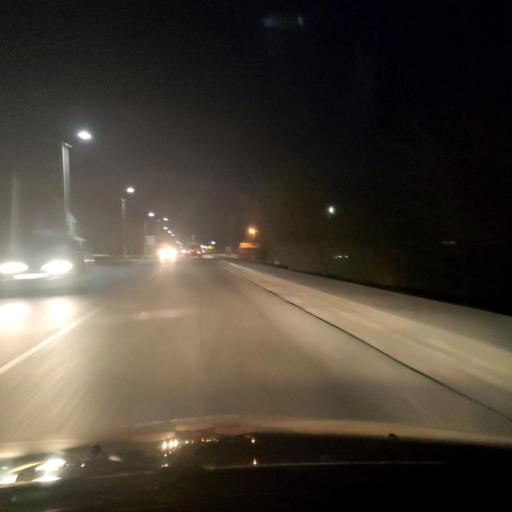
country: RU
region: Voronezj
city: Novaya Usman'
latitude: 51.6276
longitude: 39.4001
